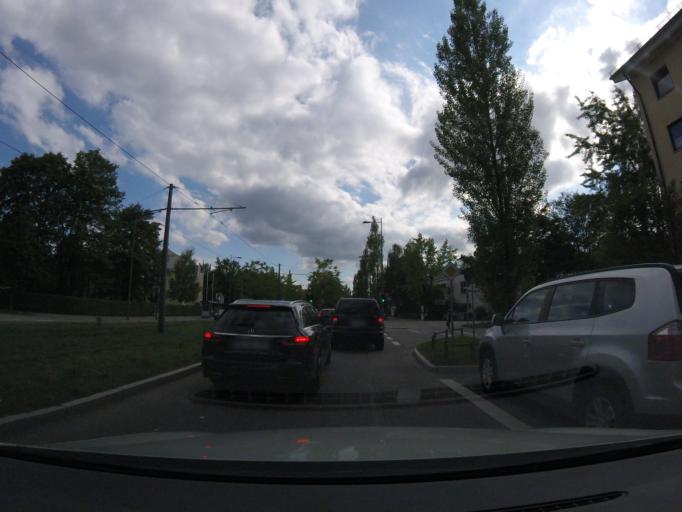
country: DE
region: Bavaria
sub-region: Upper Bavaria
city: Unterfoehring
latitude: 48.1705
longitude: 11.6354
